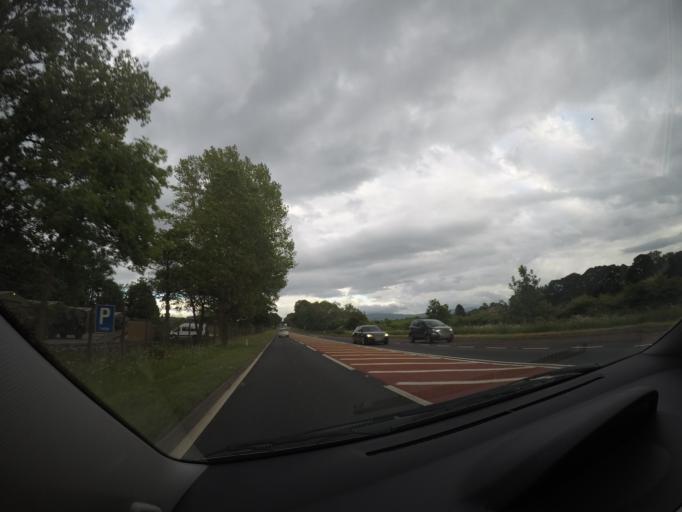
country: GB
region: England
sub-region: Cumbria
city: Kirkby Stephen
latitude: 54.5382
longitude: -2.3831
